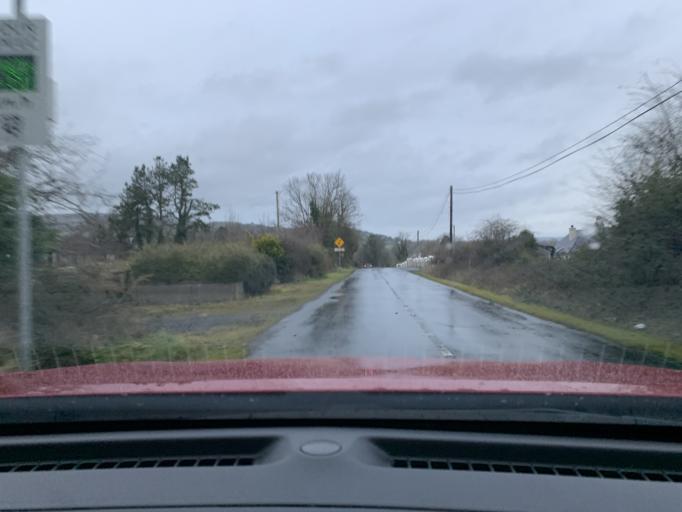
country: IE
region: Connaught
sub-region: Roscommon
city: Boyle
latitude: 54.0237
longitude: -8.3288
